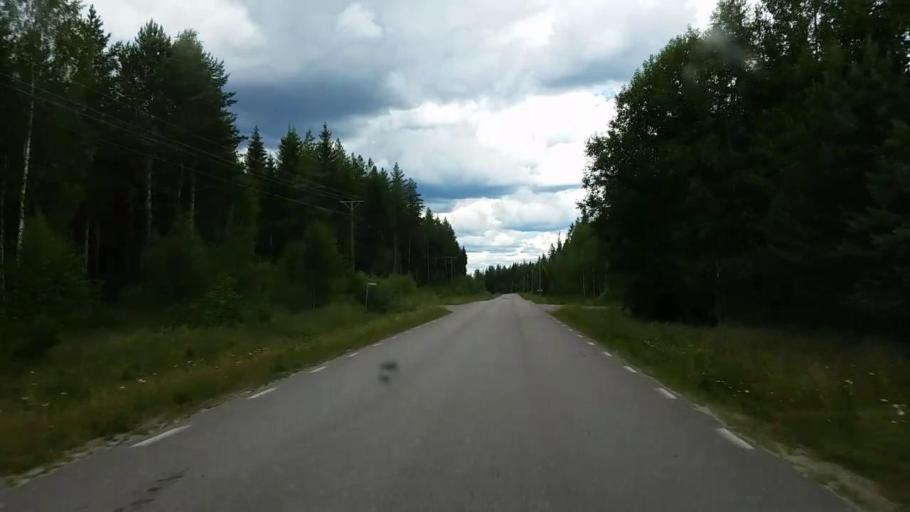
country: SE
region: Gaevleborg
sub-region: Ovanakers Kommun
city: Edsbyn
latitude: 61.4289
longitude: 15.8991
